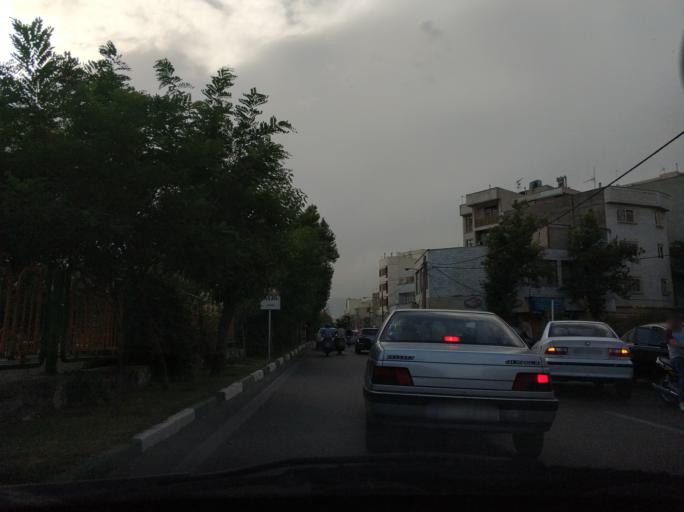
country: IR
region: Tehran
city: Tehran
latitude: 35.7166
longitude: 51.4806
